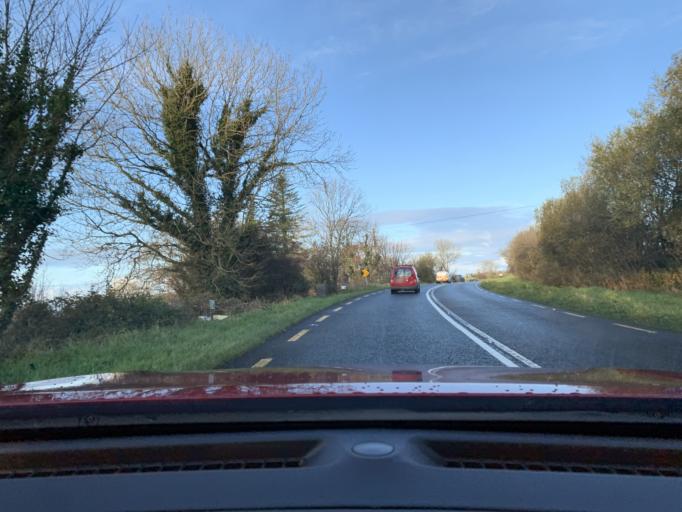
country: IE
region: Connaught
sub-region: Sligo
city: Sligo
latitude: 54.3542
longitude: -8.5130
